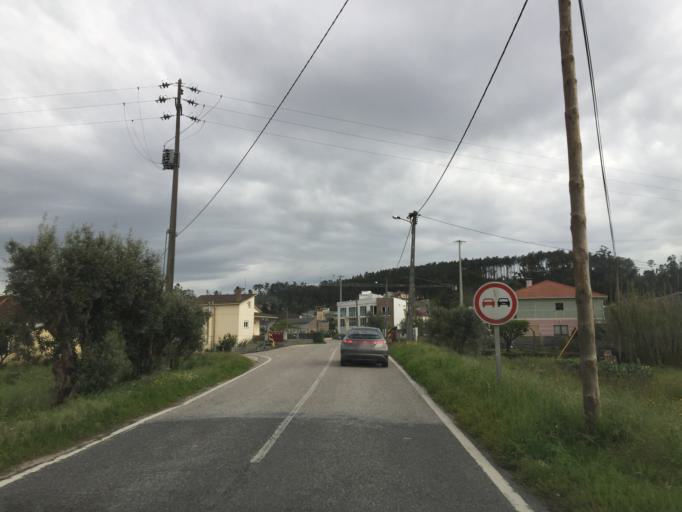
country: PT
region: Leiria
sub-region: Leiria
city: Caranguejeira
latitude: 39.7180
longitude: -8.6958
